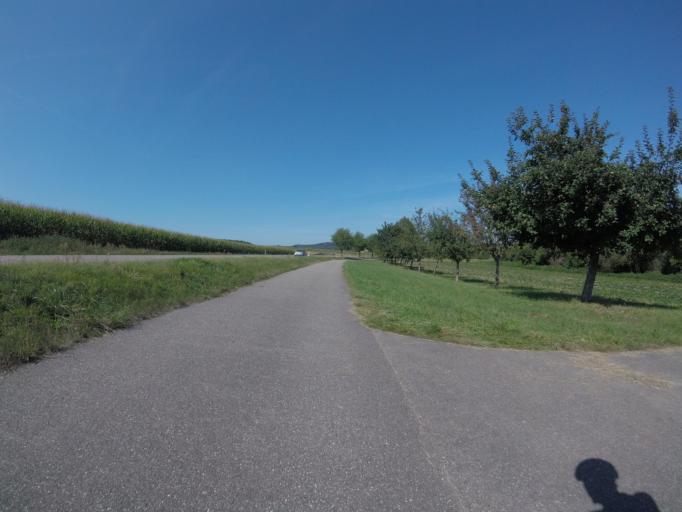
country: DE
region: Baden-Wuerttemberg
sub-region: Regierungsbezirk Stuttgart
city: Grossbottwar
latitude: 49.0082
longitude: 9.2792
